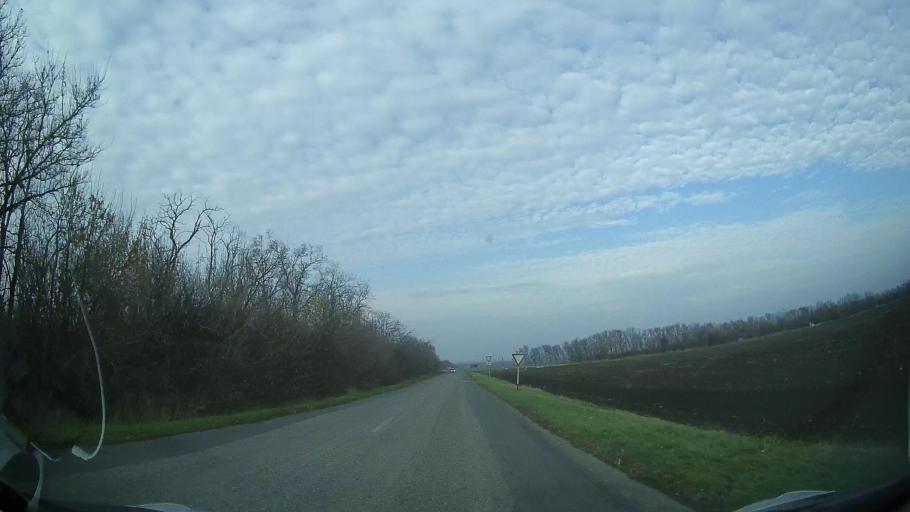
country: RU
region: Rostov
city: Bagayevskaya
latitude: 47.0897
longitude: 40.3915
